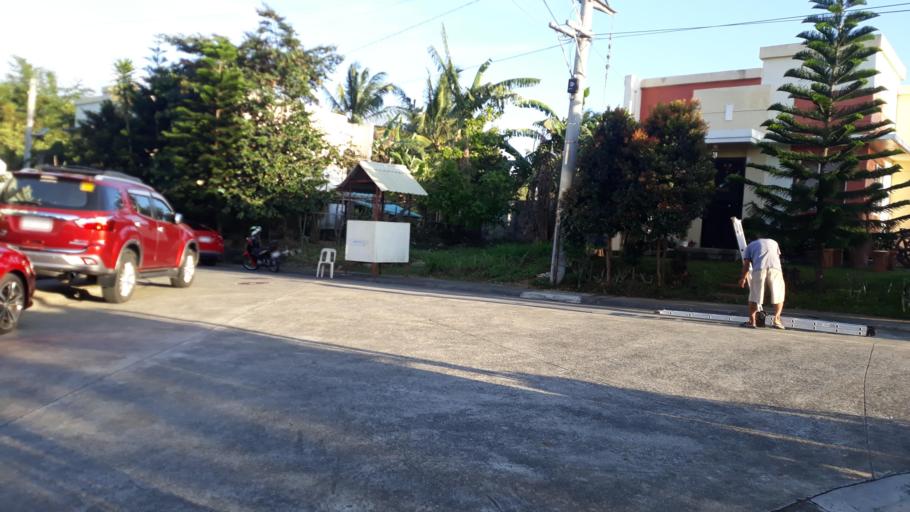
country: PH
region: Calabarzon
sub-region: Province of Cavite
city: Biga
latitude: 14.2749
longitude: 120.9715
